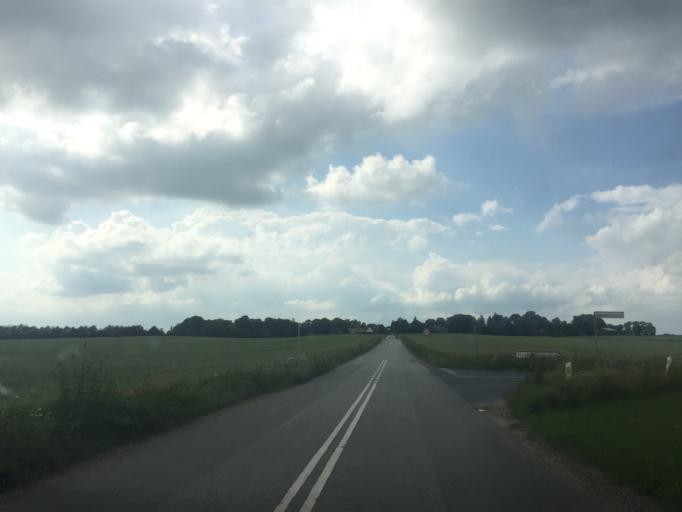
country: DK
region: Capital Region
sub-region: Hoje-Taastrup Kommune
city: Flong
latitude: 55.6891
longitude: 12.1739
